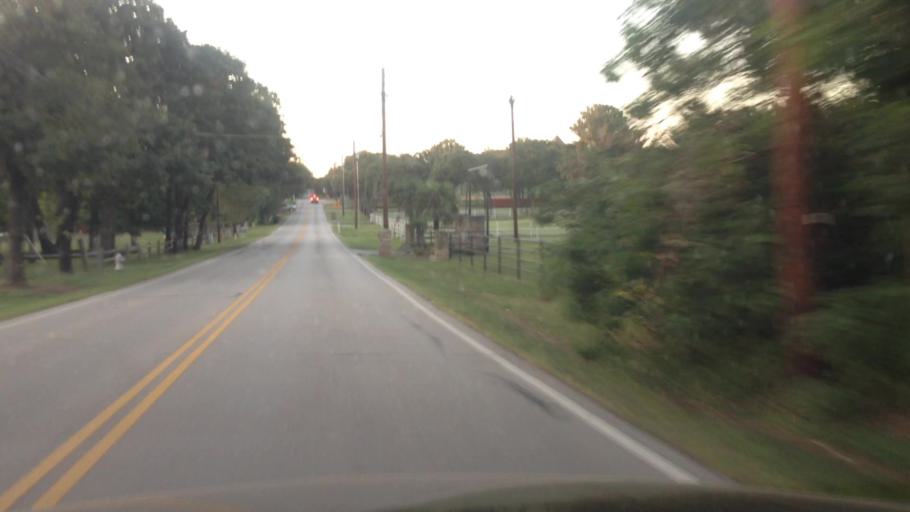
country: US
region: Texas
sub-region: Tarrant County
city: Keller
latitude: 32.9462
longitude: -97.2031
